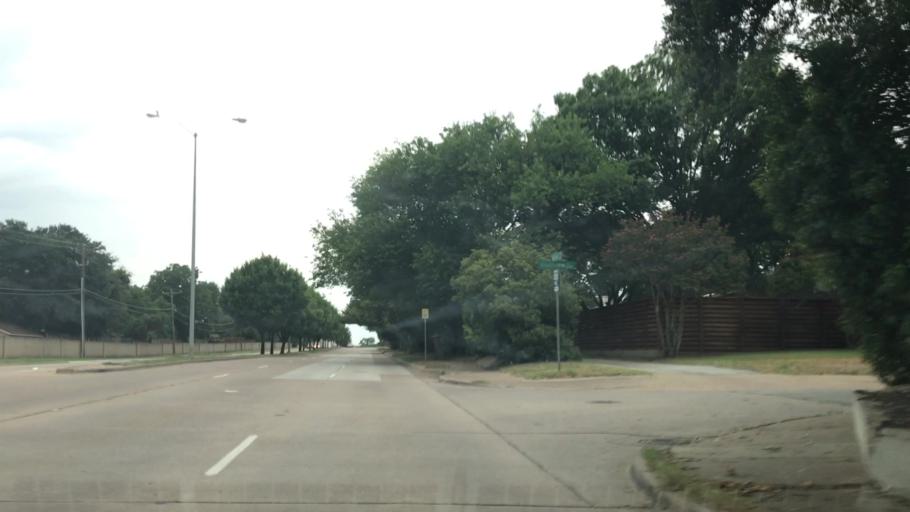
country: US
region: Texas
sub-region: Dallas County
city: Addison
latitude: 32.9501
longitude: -96.7868
